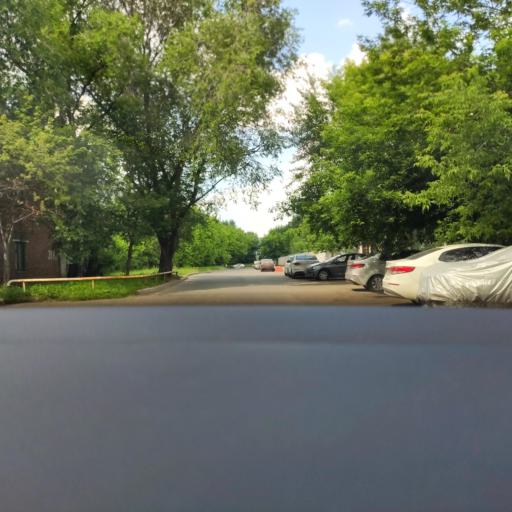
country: RU
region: Moscow
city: Slobodka
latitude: 55.8604
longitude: 37.5786
